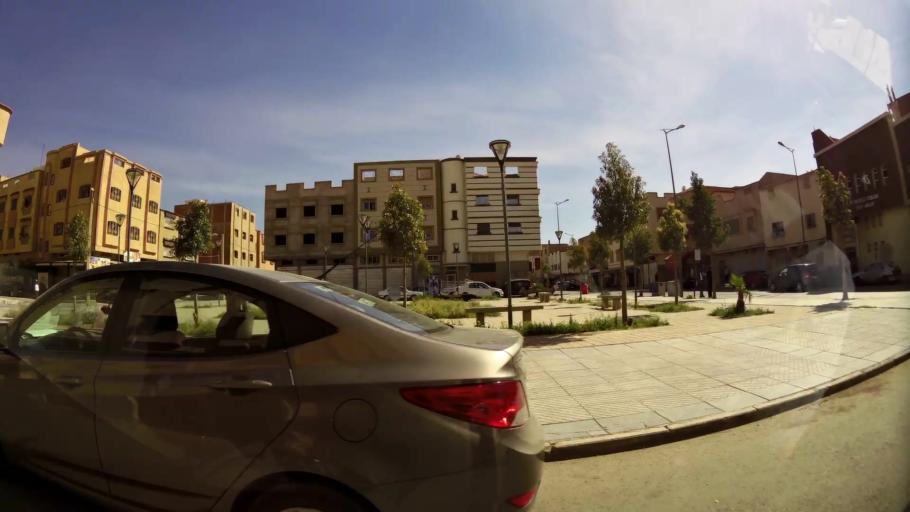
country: MA
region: Oriental
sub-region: Oujda-Angad
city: Oujda
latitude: 34.6599
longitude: -1.9204
